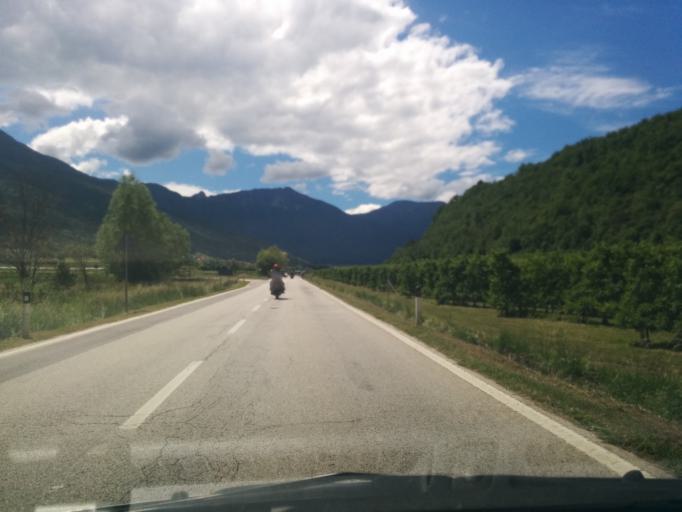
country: IT
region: Trentino-Alto Adige
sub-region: Provincia di Trento
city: Lasino
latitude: 46.0179
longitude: 10.9817
